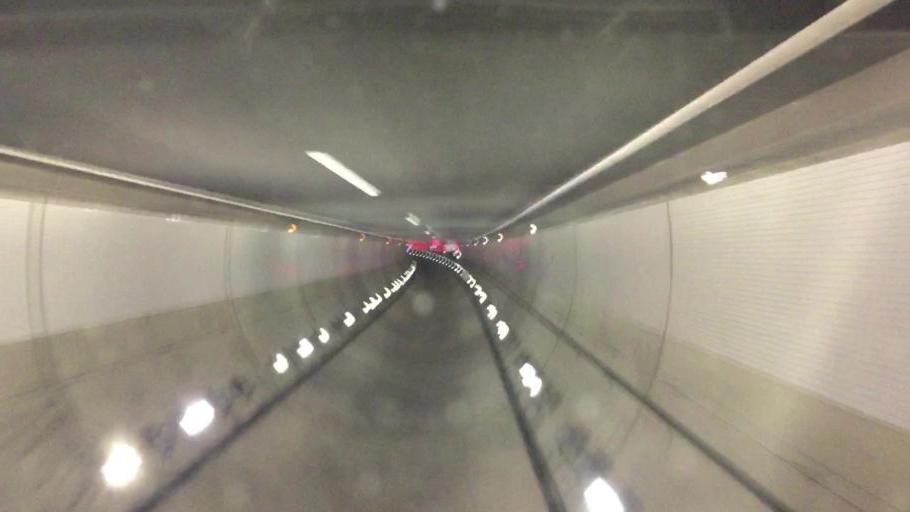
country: JP
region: Tochigi
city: Ashikaga
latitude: 36.3635
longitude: 139.4440
